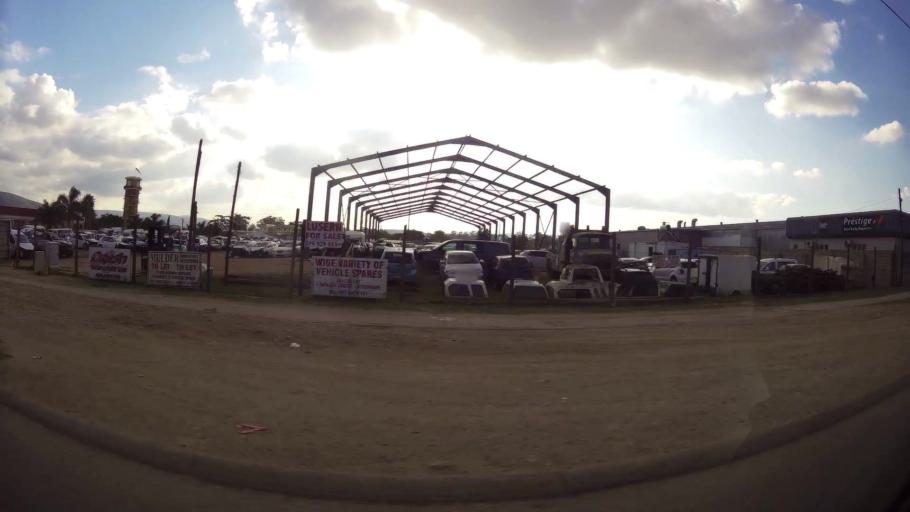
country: ZA
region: Eastern Cape
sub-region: Nelson Mandela Bay Metropolitan Municipality
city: Uitenhage
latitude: -33.7679
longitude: 25.3901
